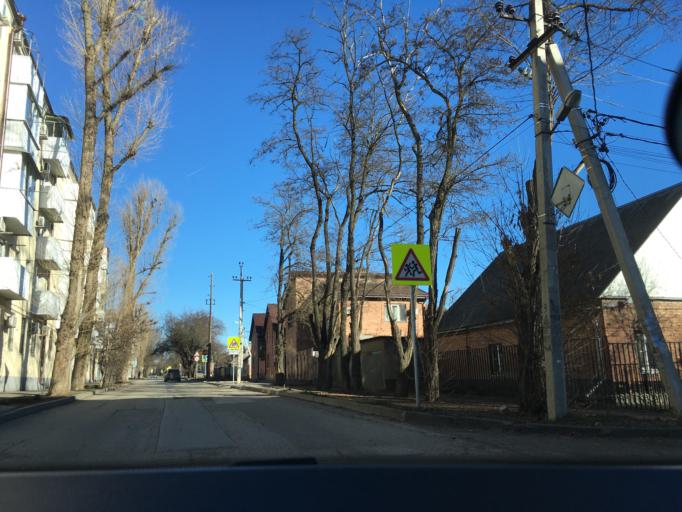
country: RU
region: Rostov
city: Imeni Chkalova
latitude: 47.2674
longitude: 39.7900
